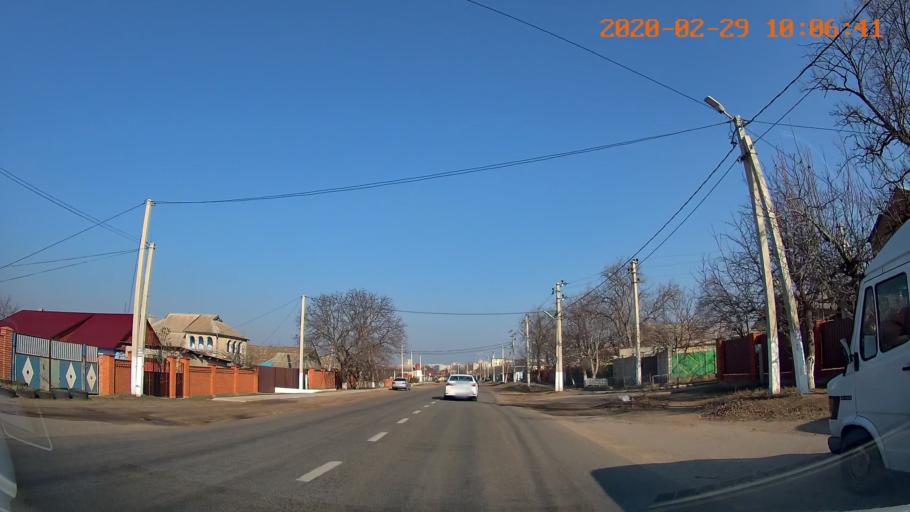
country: MD
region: Telenesti
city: Tiraspolul Nou
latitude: 46.8166
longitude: 29.6688
